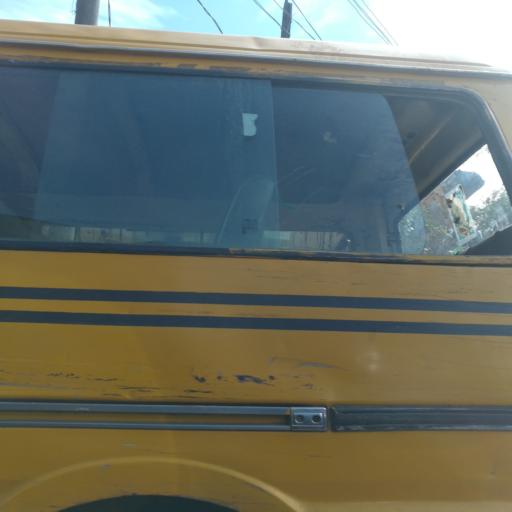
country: NG
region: Lagos
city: Lagos
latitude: 6.4594
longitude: 3.3932
